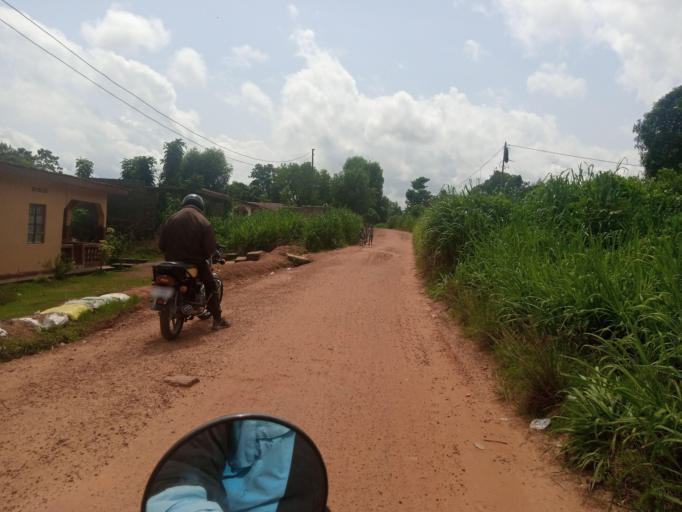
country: SL
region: Southern Province
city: Bo
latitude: 7.9624
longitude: -11.7503
